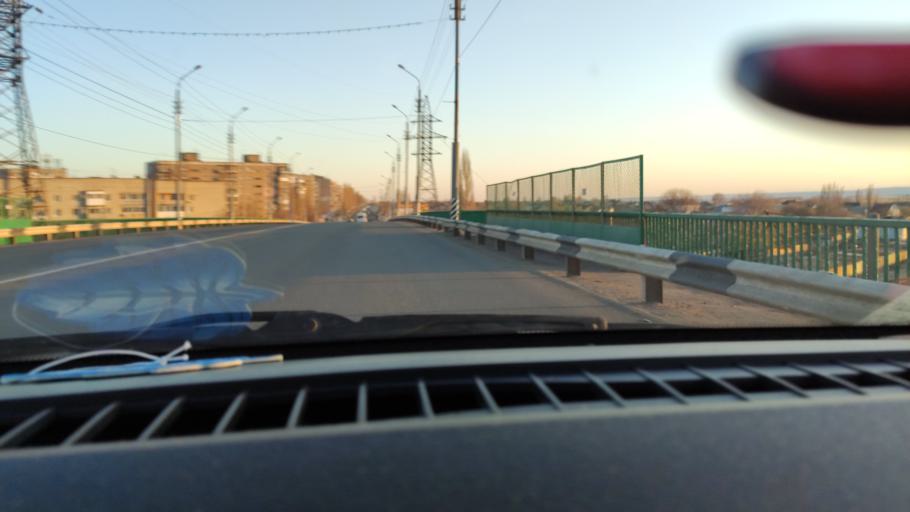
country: RU
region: Saratov
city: Privolzhskiy
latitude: 51.4131
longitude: 46.0430
